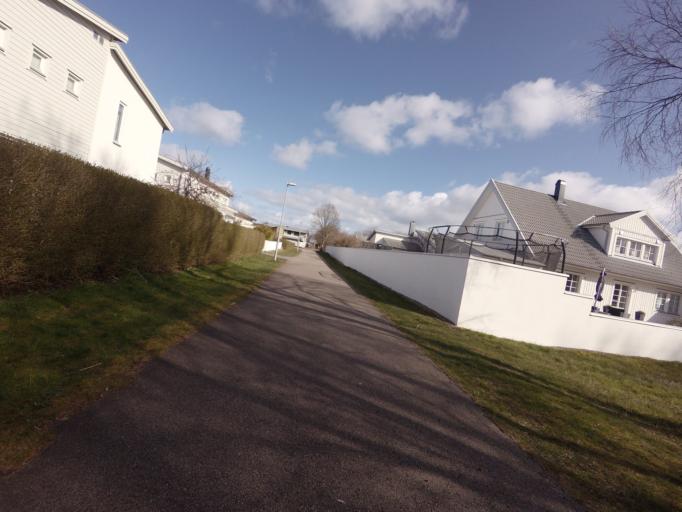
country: SE
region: Skane
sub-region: Hoganas Kommun
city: Hoganas
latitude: 56.1786
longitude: 12.5734
